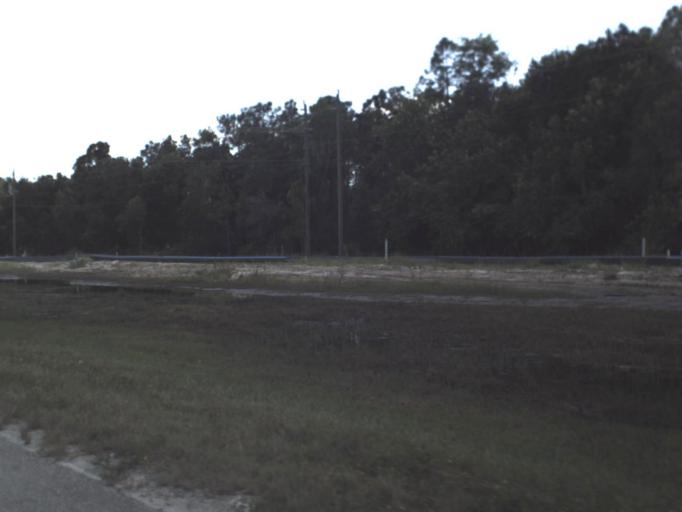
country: US
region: Florida
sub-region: Collier County
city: Lely Resort
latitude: 26.0602
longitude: -81.6942
